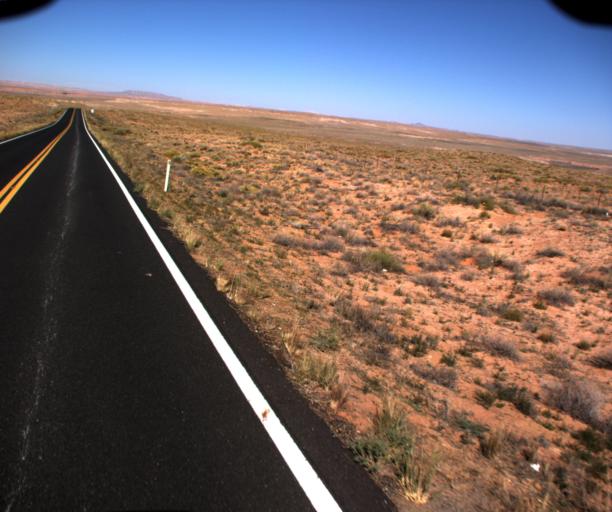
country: US
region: Arizona
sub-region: Coconino County
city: Tuba City
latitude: 36.0790
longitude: -111.1858
